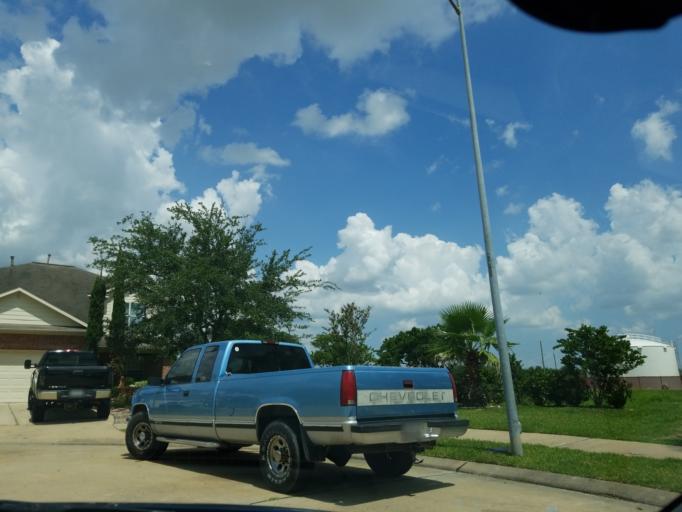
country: US
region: Texas
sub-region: Harris County
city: Cypress
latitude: 29.8766
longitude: -95.7253
